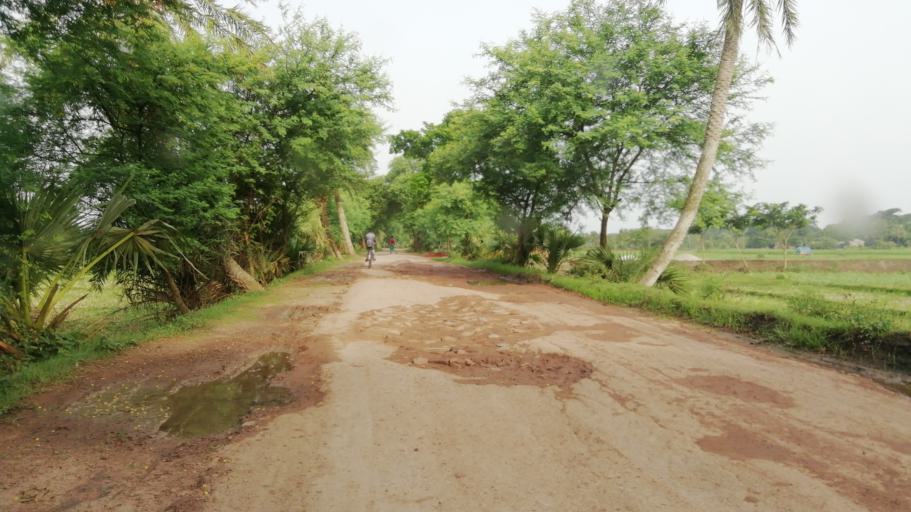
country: BD
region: Khulna
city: Bhatpara Abhaynagar
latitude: 23.0401
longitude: 89.3136
